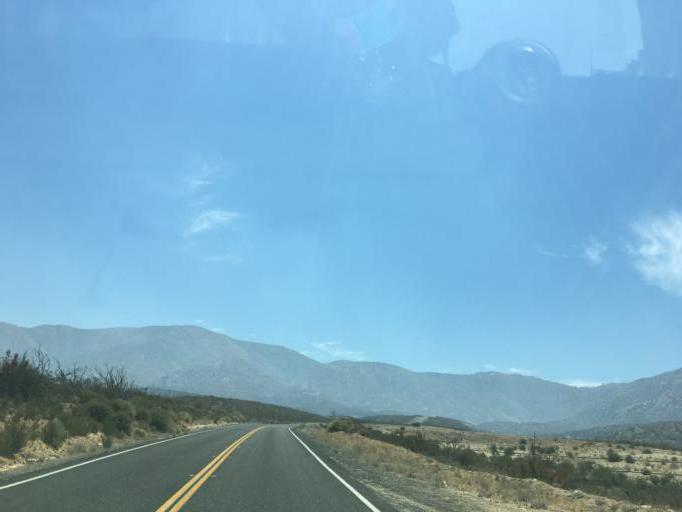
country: US
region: California
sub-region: Los Angeles County
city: Vincent
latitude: 34.4272
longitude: -118.1095
